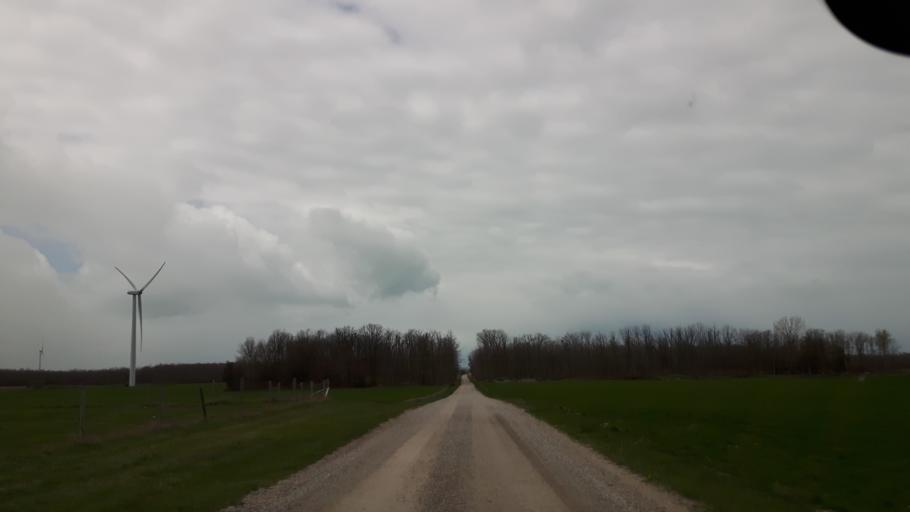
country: CA
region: Ontario
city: Bluewater
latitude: 43.4723
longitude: -81.6657
